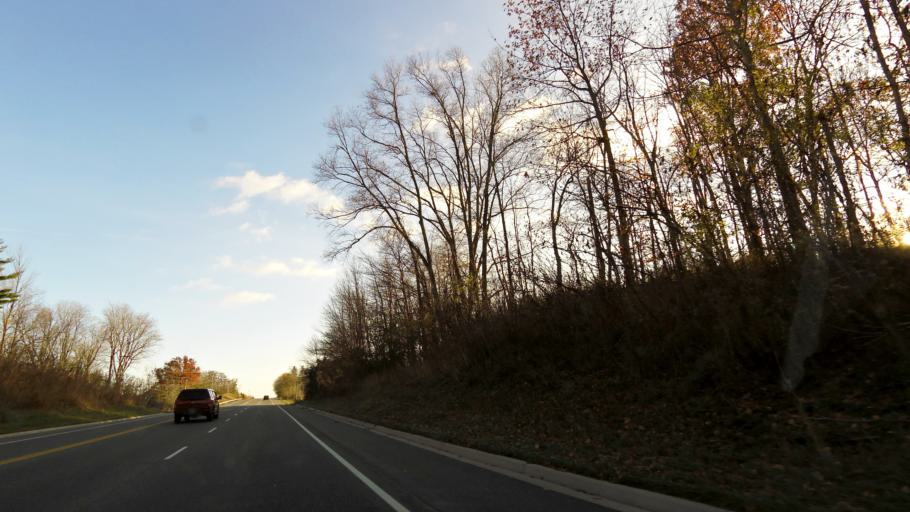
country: CA
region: Ontario
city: Cambridge
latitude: 43.2885
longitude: -80.3093
